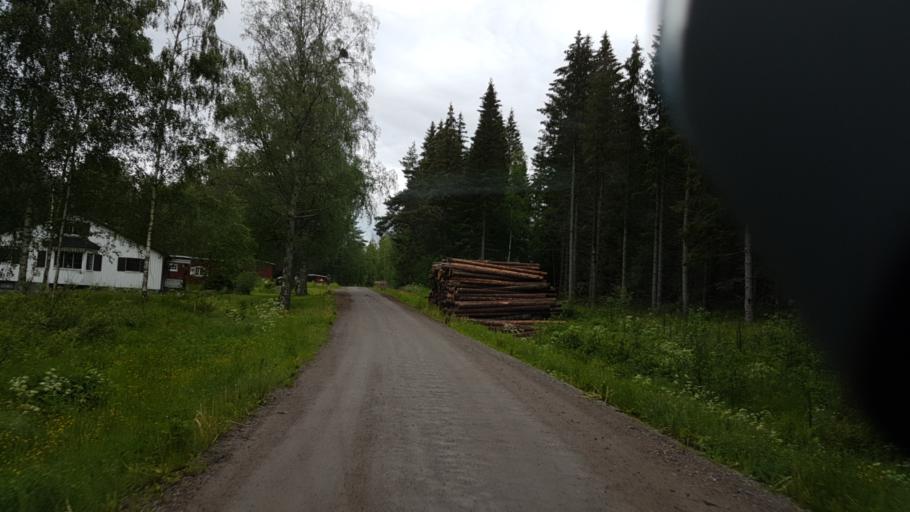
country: NO
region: Ostfold
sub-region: Romskog
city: Romskog
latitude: 59.7014
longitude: 12.0609
